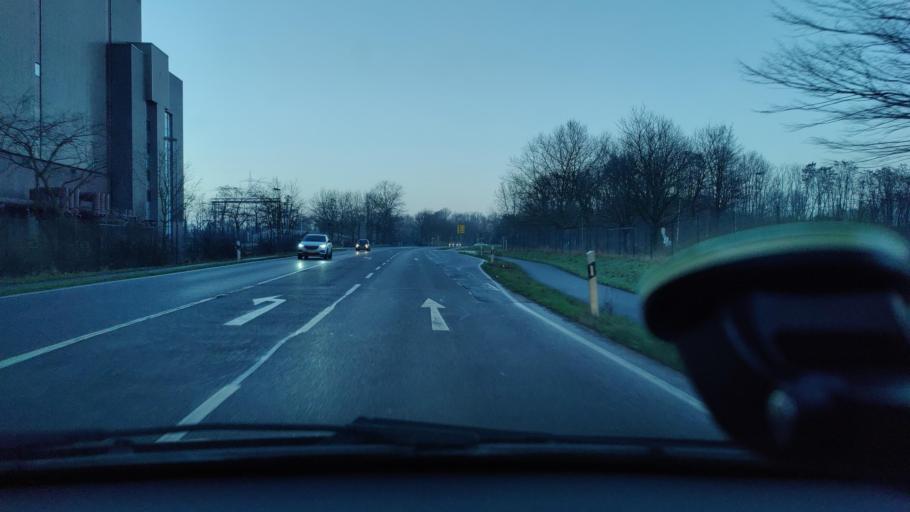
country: DE
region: North Rhine-Westphalia
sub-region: Regierungsbezirk Dusseldorf
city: Voerde
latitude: 51.5783
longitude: 6.6834
